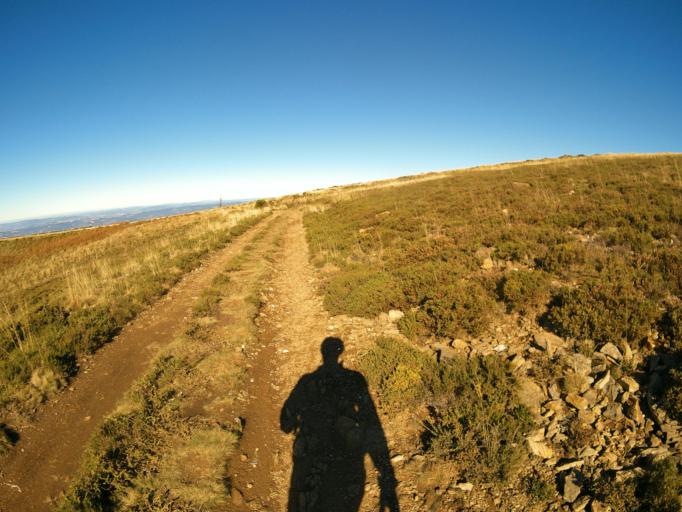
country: PT
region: Vila Real
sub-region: Mesao Frio
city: Mesao Frio
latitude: 41.2328
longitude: -7.9156
